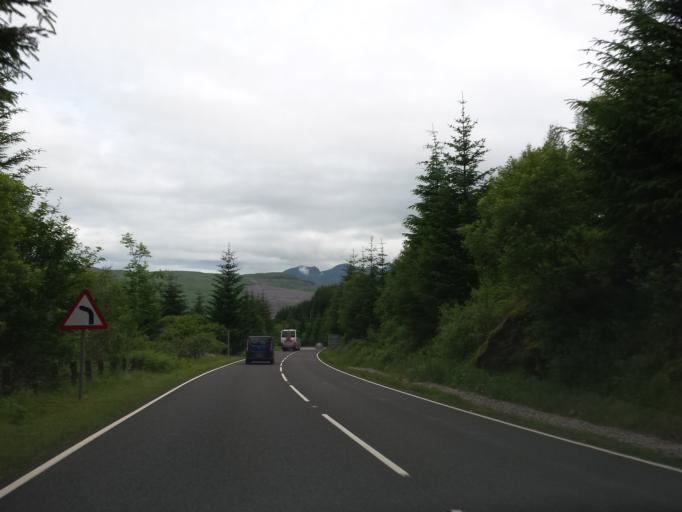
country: GB
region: Scotland
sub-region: Stirling
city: Callander
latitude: 56.4276
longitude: -4.3401
